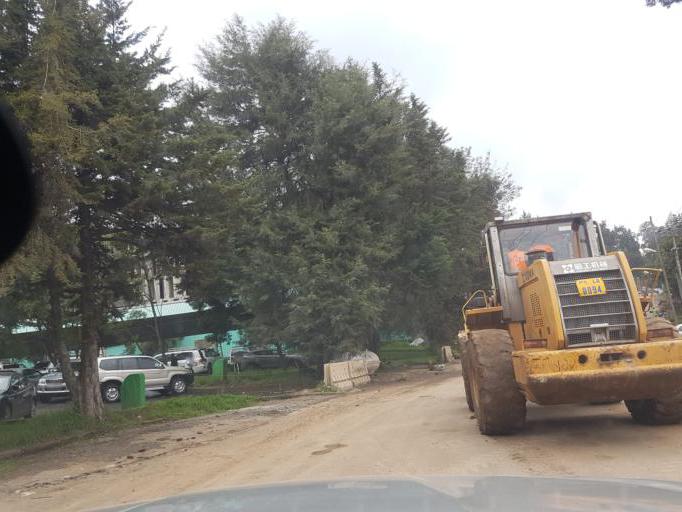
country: ET
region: Adis Abeba
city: Addis Ababa
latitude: 9.0271
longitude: 38.7663
